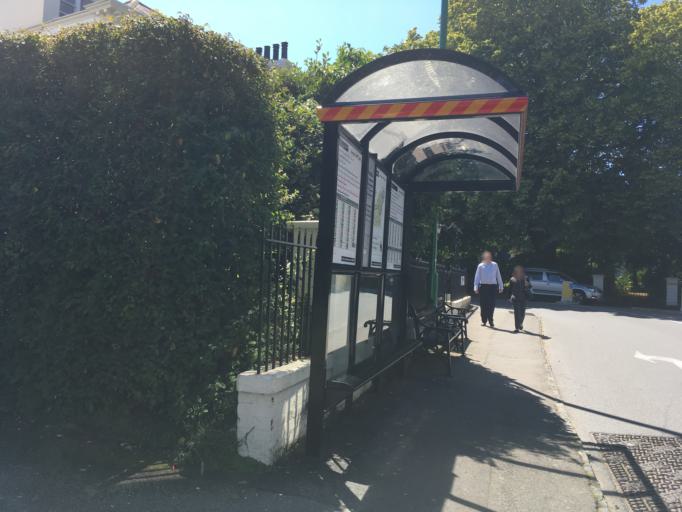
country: GG
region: St Peter Port
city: Saint Peter Port
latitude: 49.4558
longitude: -2.5477
